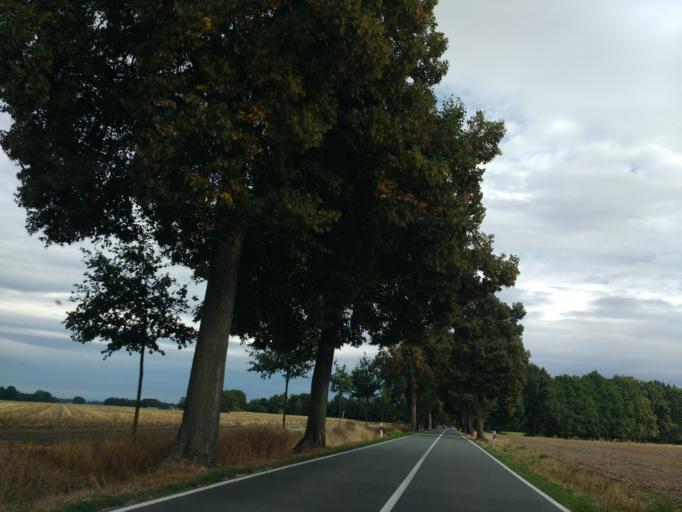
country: DE
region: North Rhine-Westphalia
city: Rietberg
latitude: 51.8251
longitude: 8.4600
